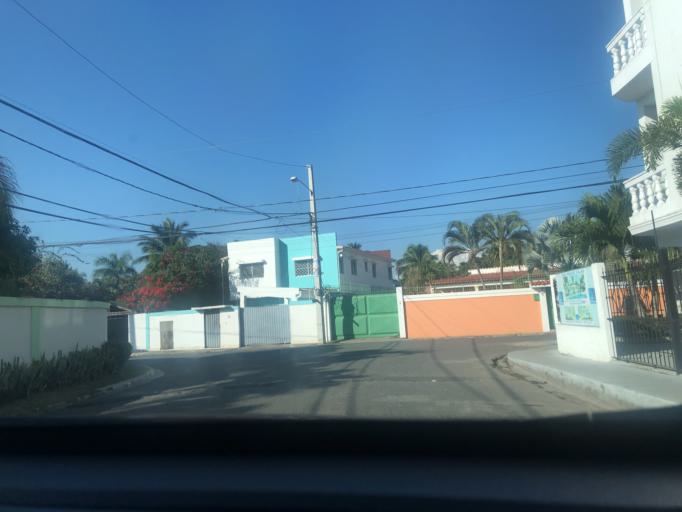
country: DO
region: Santo Domingo
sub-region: Santo Domingo
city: Boca Chica
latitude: 18.4518
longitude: -69.6065
